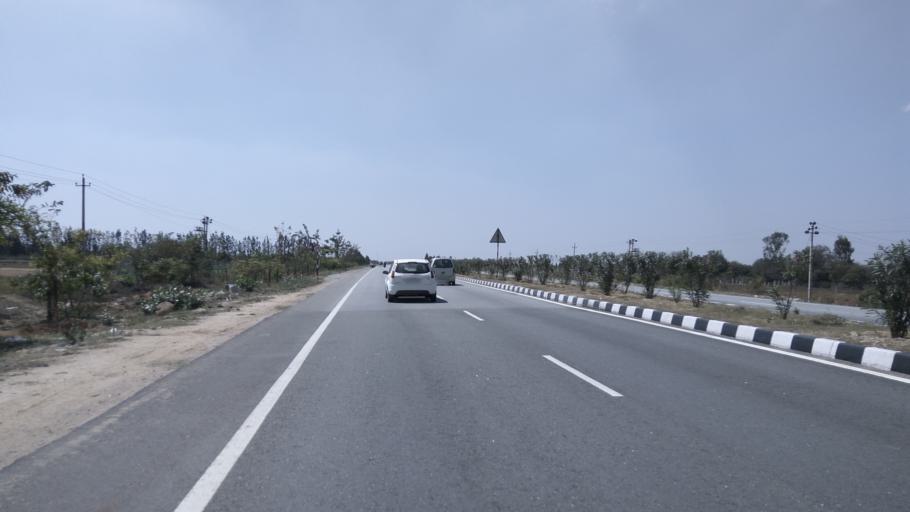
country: IN
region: Karnataka
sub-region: Kolar
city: Mulbagal
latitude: 13.1515
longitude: 78.3836
